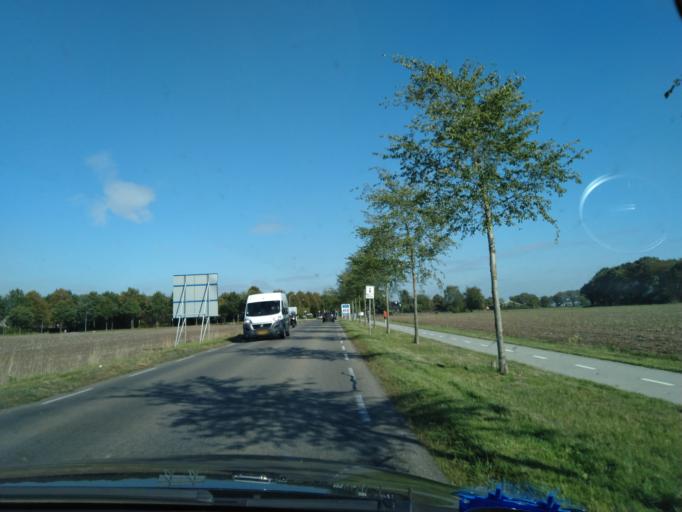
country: NL
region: Drenthe
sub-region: Gemeente Aa en Hunze
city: Anloo
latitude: 53.0496
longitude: 6.7158
